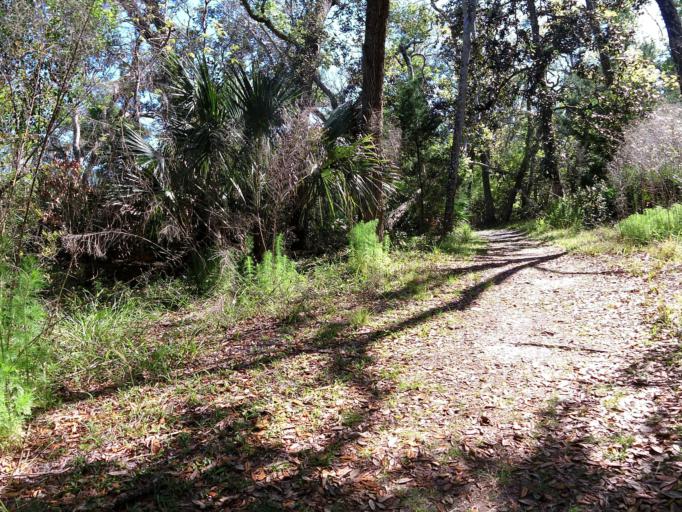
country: US
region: Florida
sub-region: Saint Johns County
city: Villano Beach
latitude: 29.9932
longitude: -81.3265
